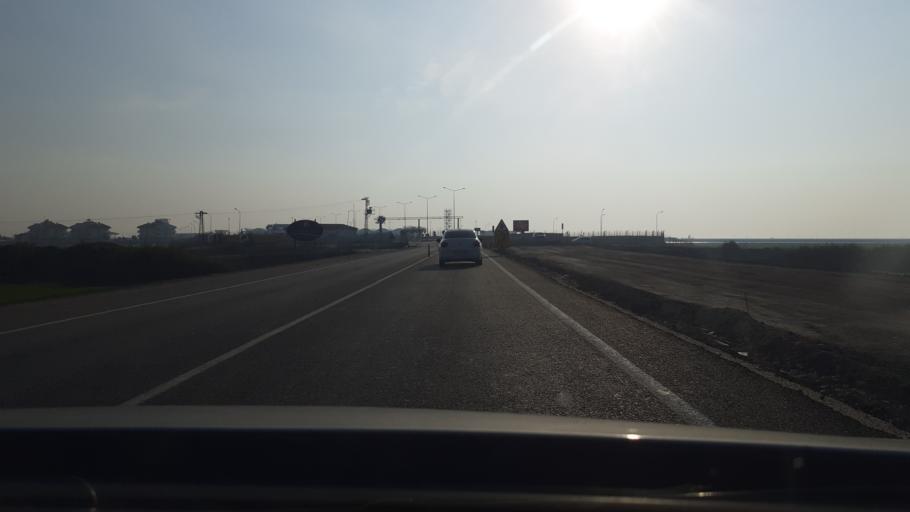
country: TR
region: Hatay
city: Serinyol
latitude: 36.3650
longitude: 36.2714
